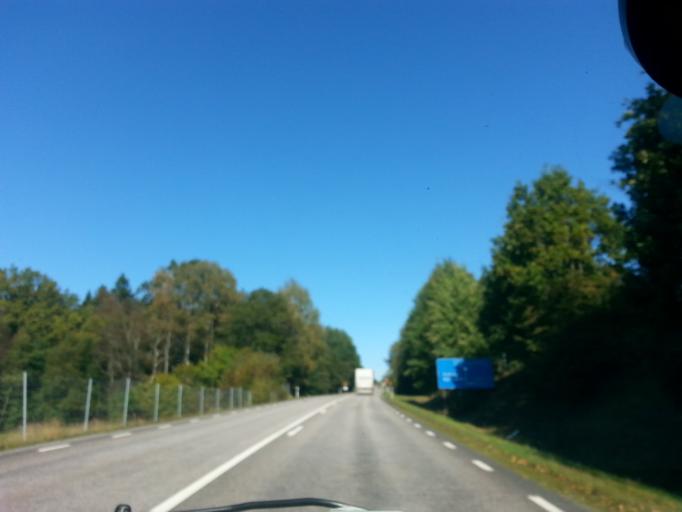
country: SE
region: Vaestra Goetaland
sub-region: Harryda Kommun
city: Ravlanda
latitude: 57.6157
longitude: 12.4347
